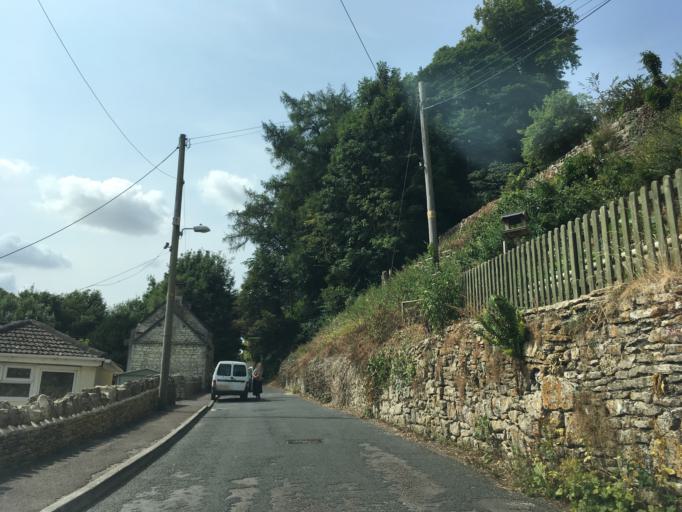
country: GB
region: England
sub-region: Gloucestershire
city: Nailsworth
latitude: 51.6921
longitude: -2.2229
